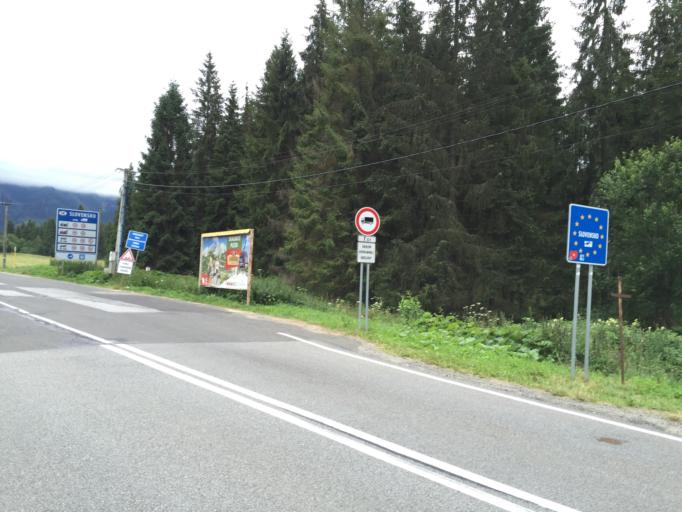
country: PL
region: Lesser Poland Voivodeship
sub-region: Powiat tatrzanski
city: Bukowina Tatrzanska
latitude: 49.3046
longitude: 20.1606
